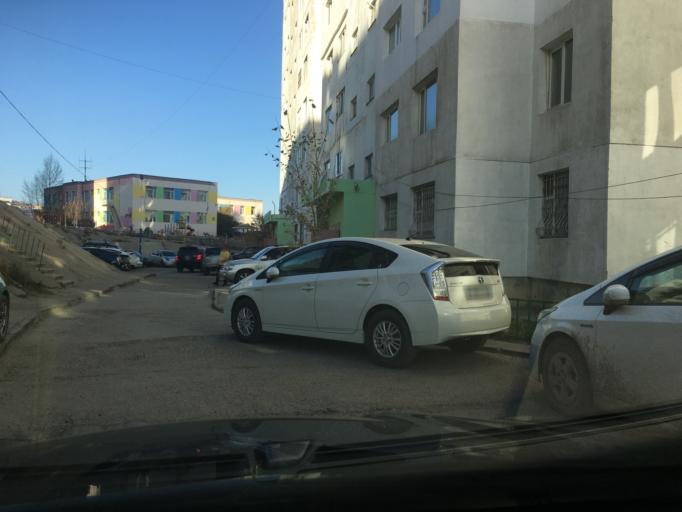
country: MN
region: Ulaanbaatar
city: Ulaanbaatar
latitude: 47.9274
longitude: 106.8817
